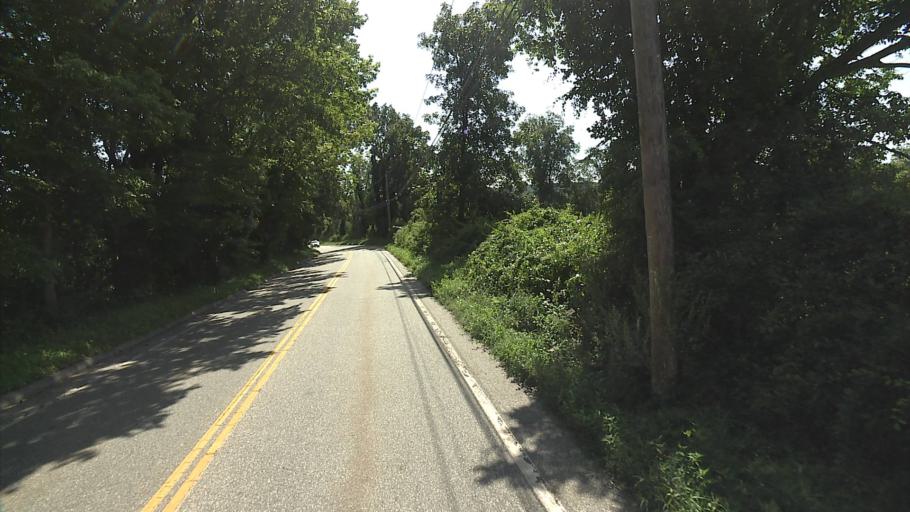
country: US
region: Connecticut
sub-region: Windham County
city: South Windham
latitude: 41.6397
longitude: -72.1796
